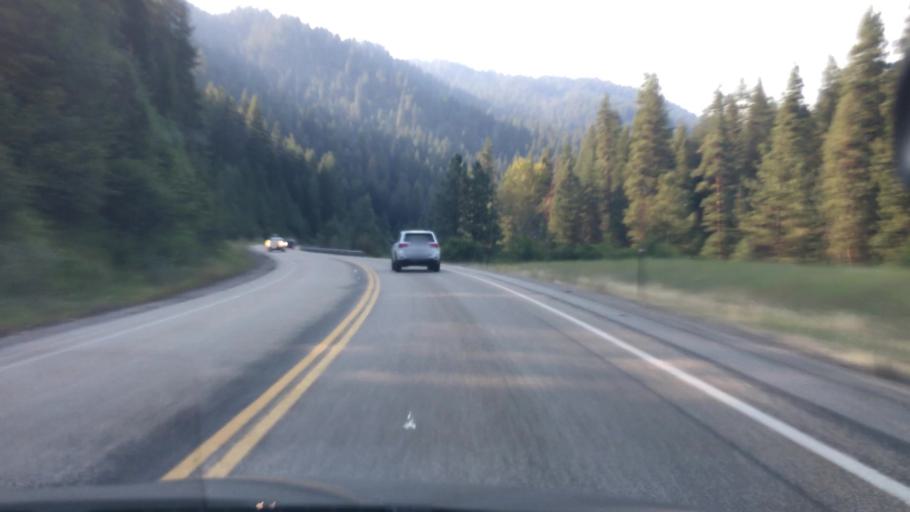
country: US
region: Idaho
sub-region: Valley County
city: Cascade
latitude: 44.1649
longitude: -116.1184
